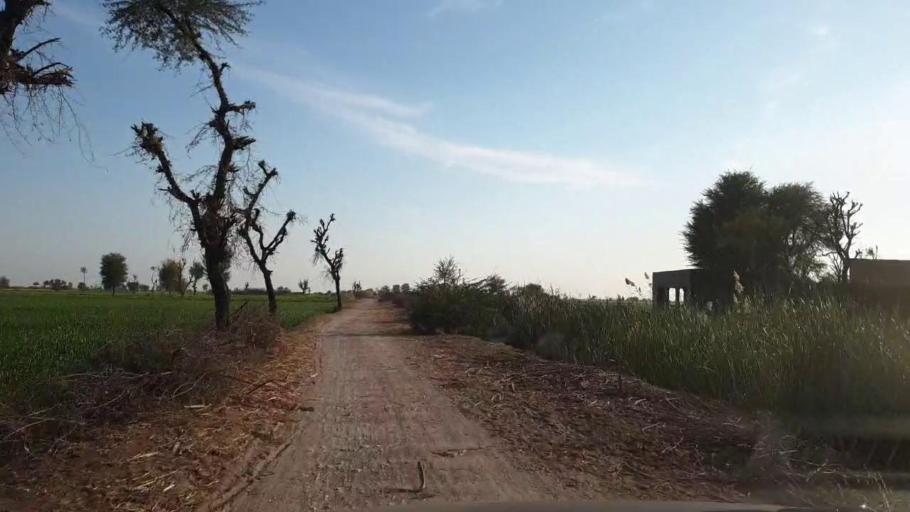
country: PK
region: Sindh
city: Khadro
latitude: 26.2207
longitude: 68.7403
